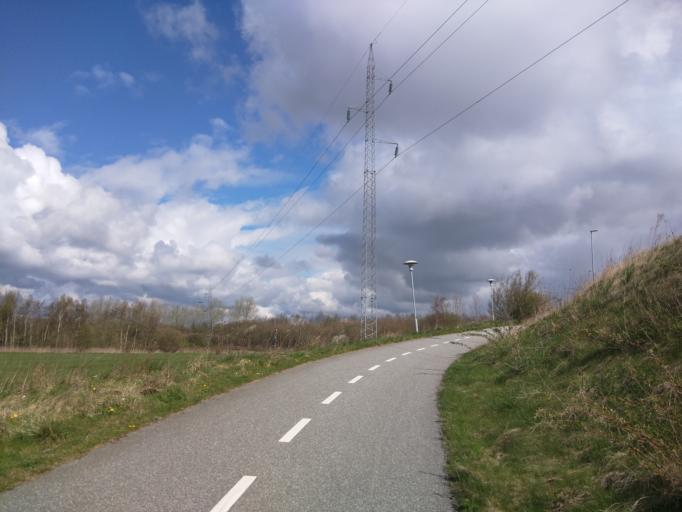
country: DK
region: South Denmark
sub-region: Fredericia Kommune
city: Snoghoj
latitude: 55.5374
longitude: 9.7063
